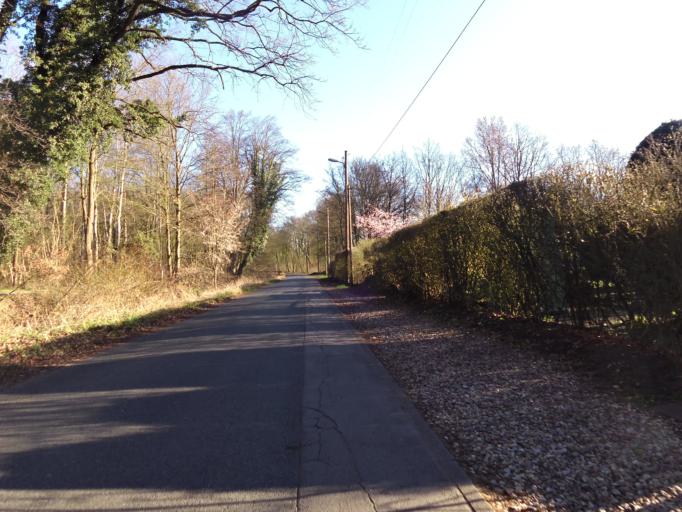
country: DE
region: Lower Saxony
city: Hannover
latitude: 52.3806
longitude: 9.7889
